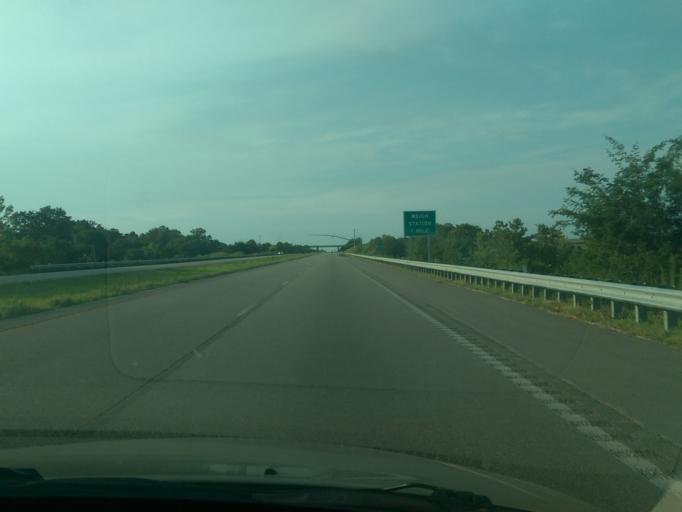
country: US
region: Missouri
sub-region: Platte County
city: Platte City
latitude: 39.4143
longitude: -94.7896
